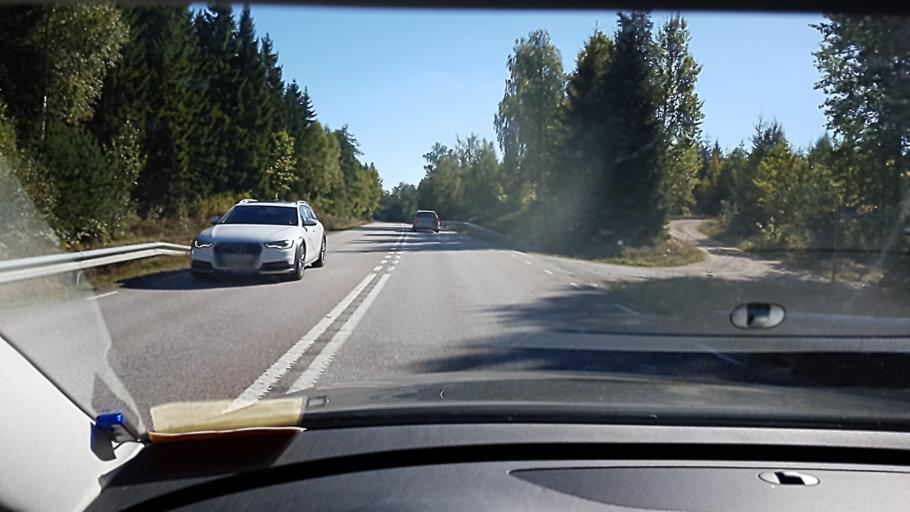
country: SE
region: Kronoberg
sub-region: Lessebo Kommun
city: Lessebo
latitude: 56.7307
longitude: 15.2965
